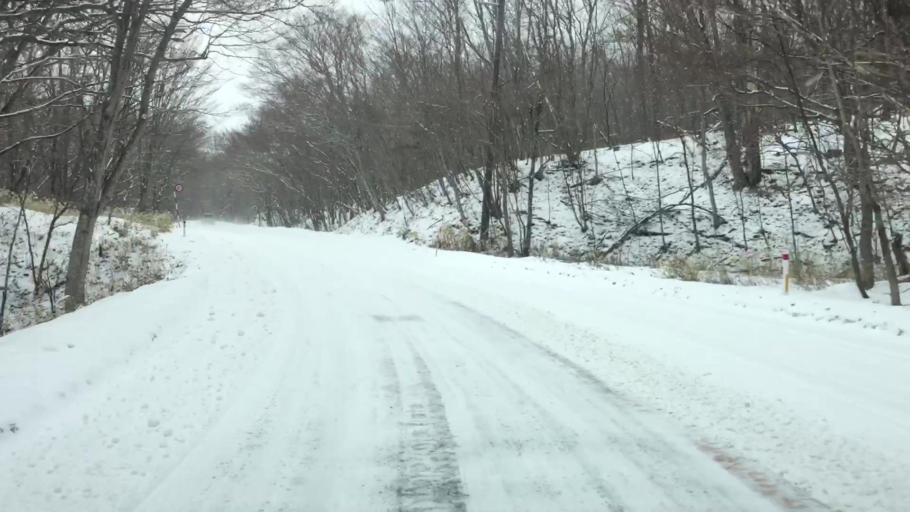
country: JP
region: Tochigi
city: Imaichi
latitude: 36.8937
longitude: 139.7400
